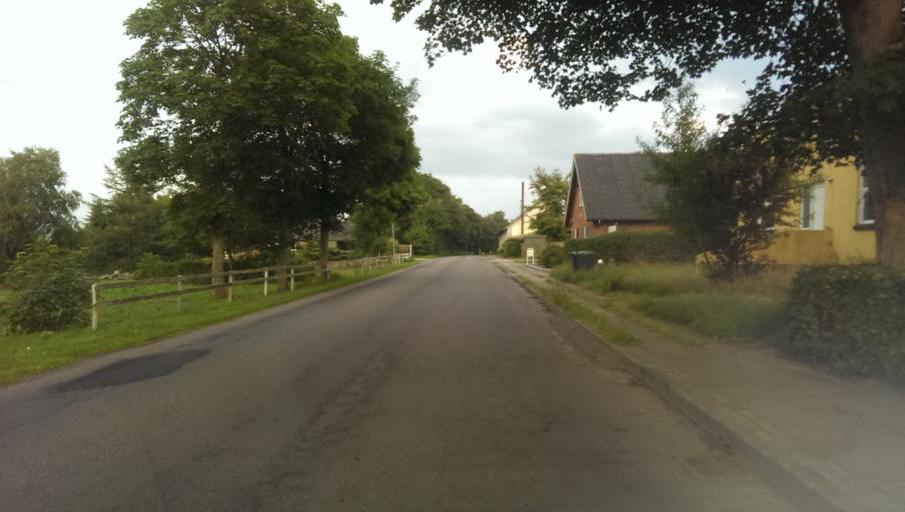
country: DK
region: South Denmark
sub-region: Esbjerg Kommune
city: Tjaereborg
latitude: 55.5542
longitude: 8.6264
